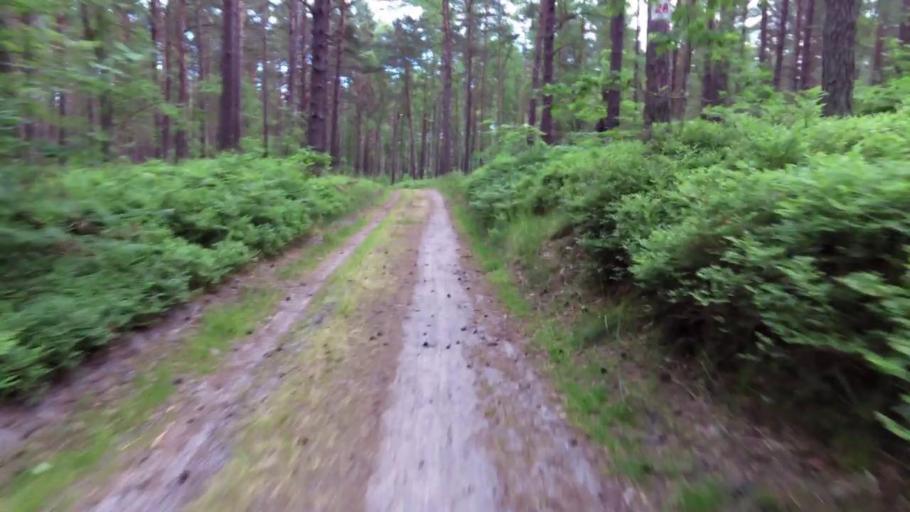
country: PL
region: West Pomeranian Voivodeship
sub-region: Powiat kamienski
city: Miedzyzdroje
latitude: 53.9073
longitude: 14.3743
